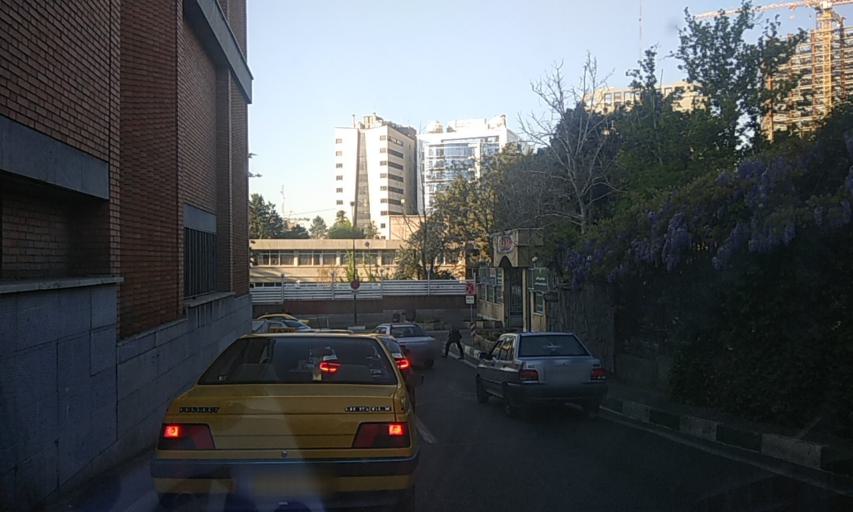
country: IR
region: Tehran
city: Tajrish
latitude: 35.7636
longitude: 51.4093
